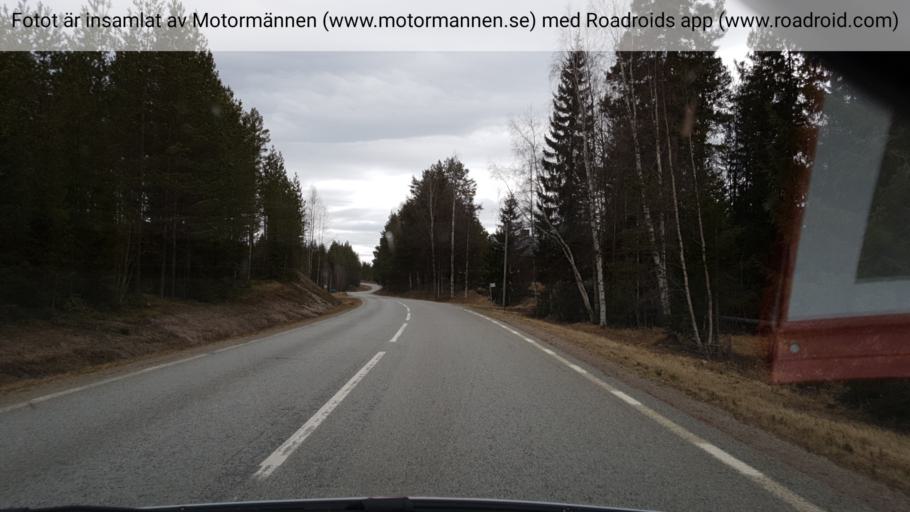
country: SE
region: Vaesterbotten
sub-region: Asele Kommun
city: Asele
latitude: 63.8358
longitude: 17.1587
